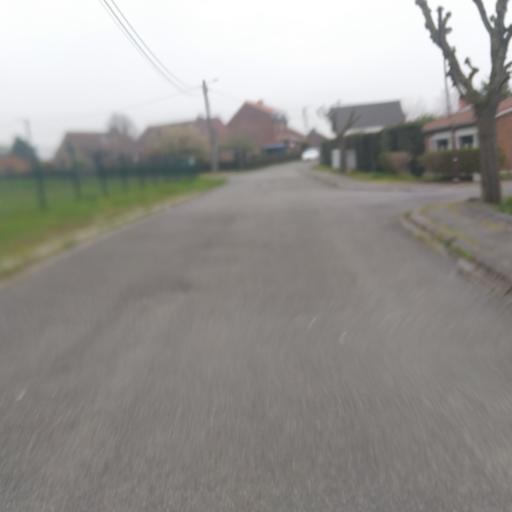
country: BE
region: Wallonia
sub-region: Province du Hainaut
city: Mons
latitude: 50.4894
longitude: 3.9577
